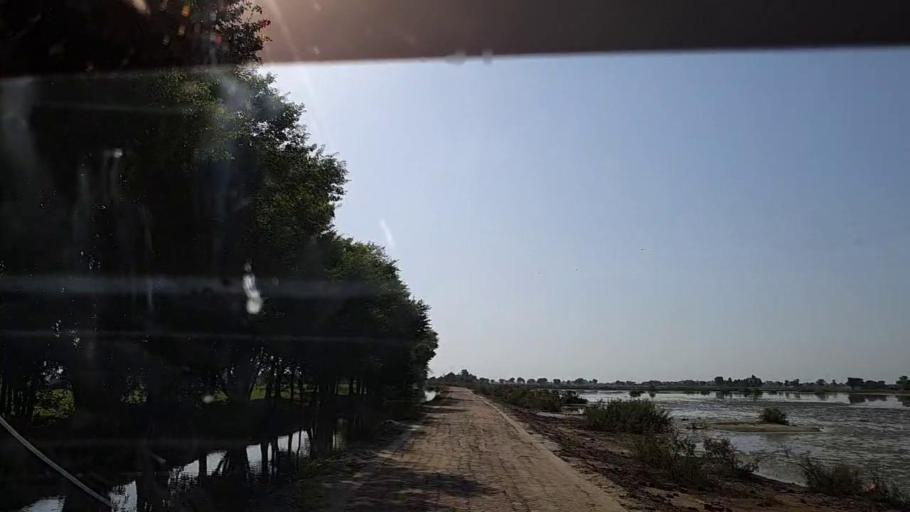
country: PK
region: Sindh
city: Tangwani
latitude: 28.2152
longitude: 68.9735
